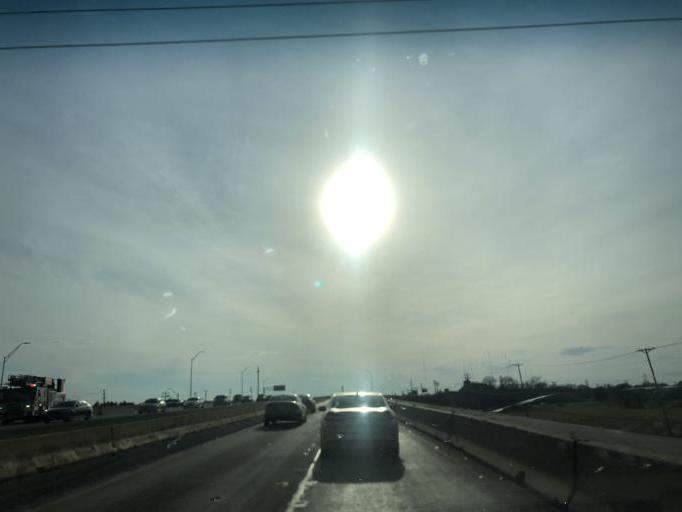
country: US
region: Texas
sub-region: Dallas County
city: Duncanville
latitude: 32.6205
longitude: -96.9136
